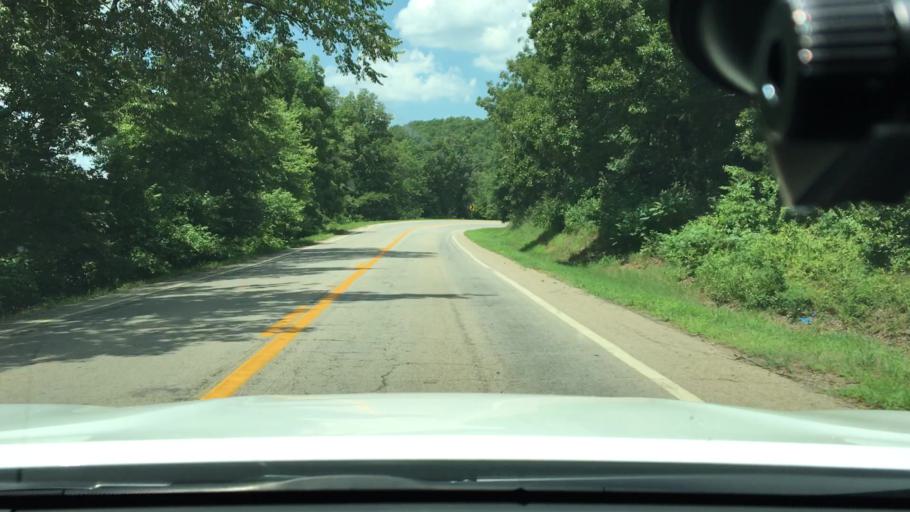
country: US
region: Arkansas
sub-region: Logan County
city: Booneville
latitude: 35.2136
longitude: -93.9383
